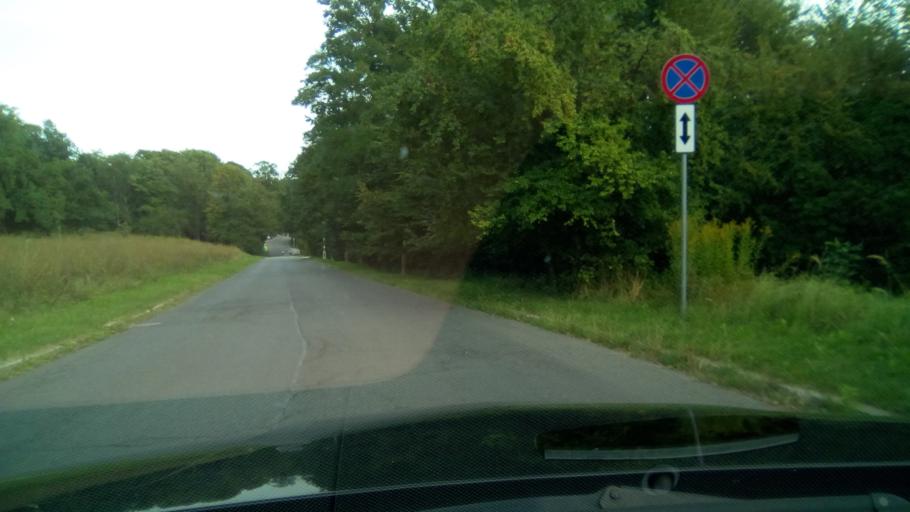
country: PL
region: Lesser Poland Voivodeship
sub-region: Krakow
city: Krakow
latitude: 50.0526
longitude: 19.8923
